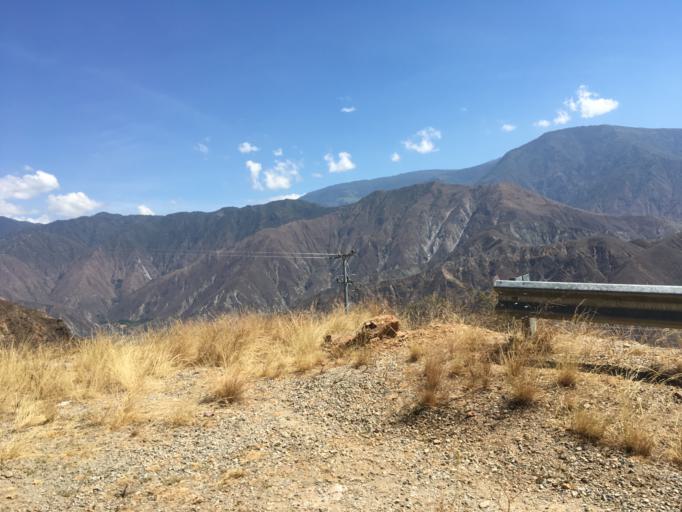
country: CO
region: Santander
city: Aratoca
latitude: 6.7882
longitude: -72.9956
